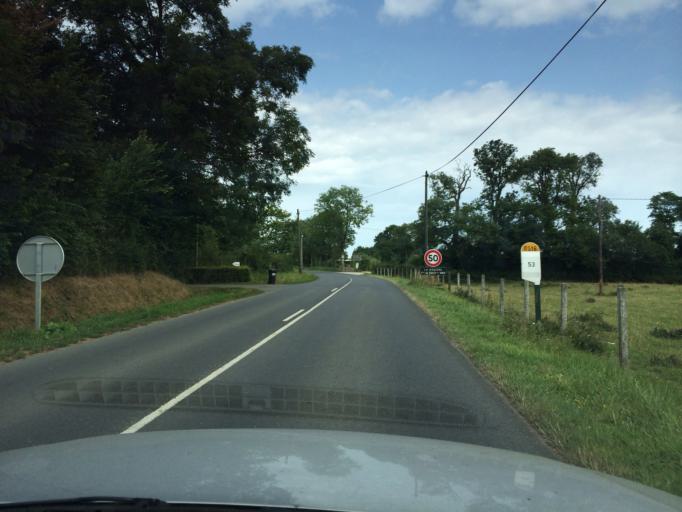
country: FR
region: Lower Normandy
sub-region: Departement du Calvados
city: Saint-Vigor-le-Grand
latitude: 49.3192
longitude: -0.6605
